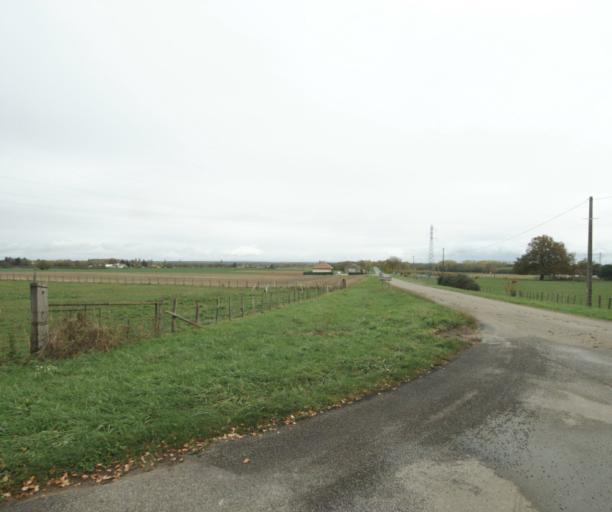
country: FR
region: Rhone-Alpes
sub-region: Departement de l'Ain
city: Pont-de-Vaux
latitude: 46.4657
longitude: 4.8855
